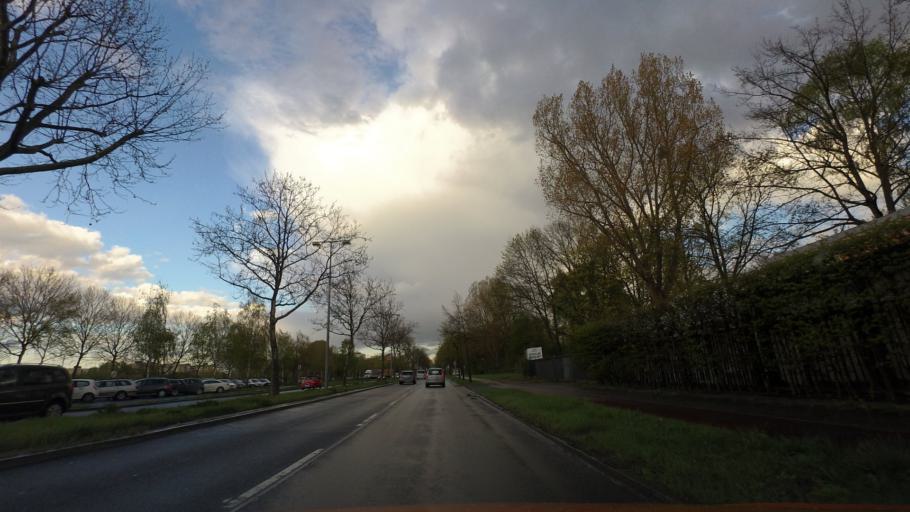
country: DE
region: Berlin
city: Staaken
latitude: 52.5231
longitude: 13.1480
